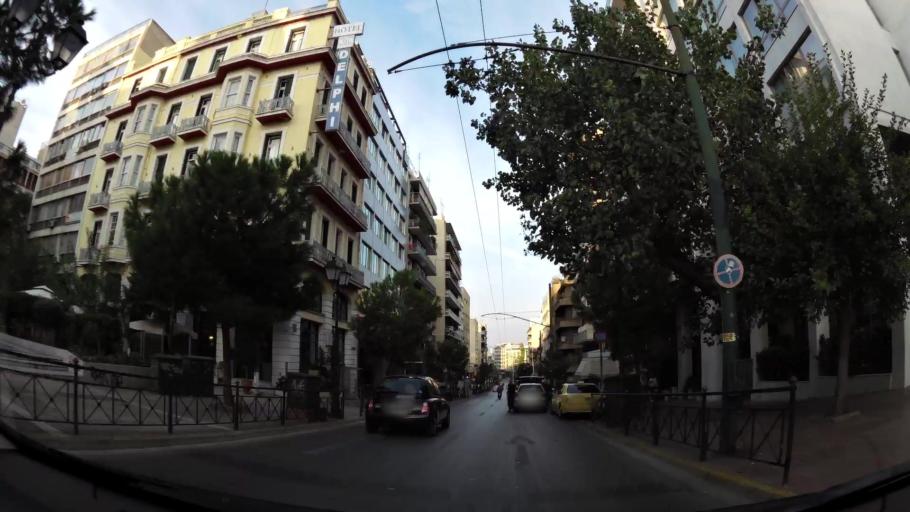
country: GR
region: Attica
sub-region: Nomarchia Athinas
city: Athens
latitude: 37.9847
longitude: 23.7248
